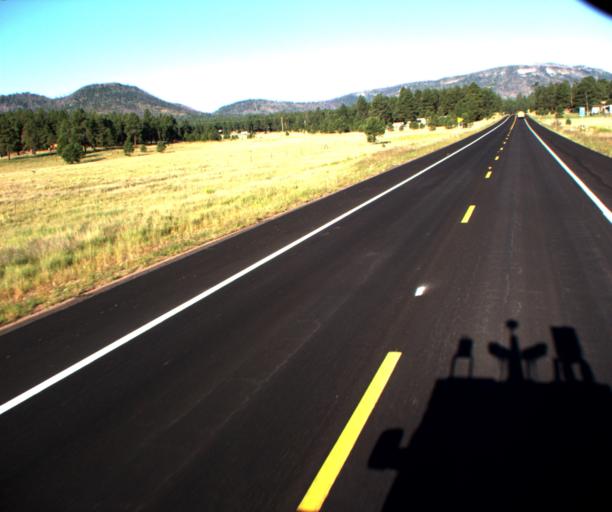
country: US
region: Arizona
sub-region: Apache County
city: Eagar
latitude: 33.8275
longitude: -109.1043
